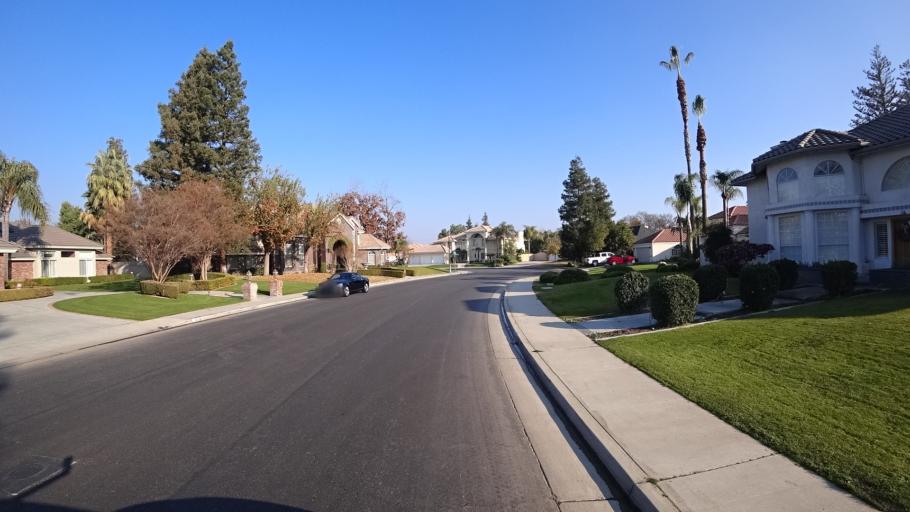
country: US
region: California
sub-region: Kern County
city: Greenacres
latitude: 35.3322
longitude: -119.1007
